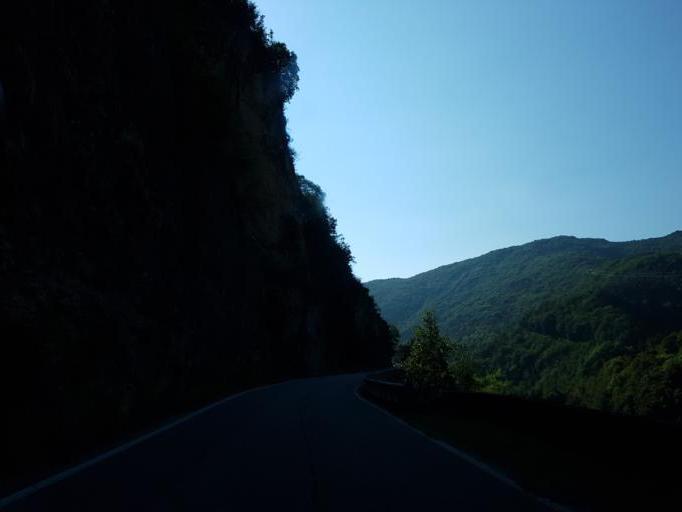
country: IT
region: Piedmont
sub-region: Provincia di Cuneo
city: Macra
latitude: 44.4939
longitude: 7.2123
